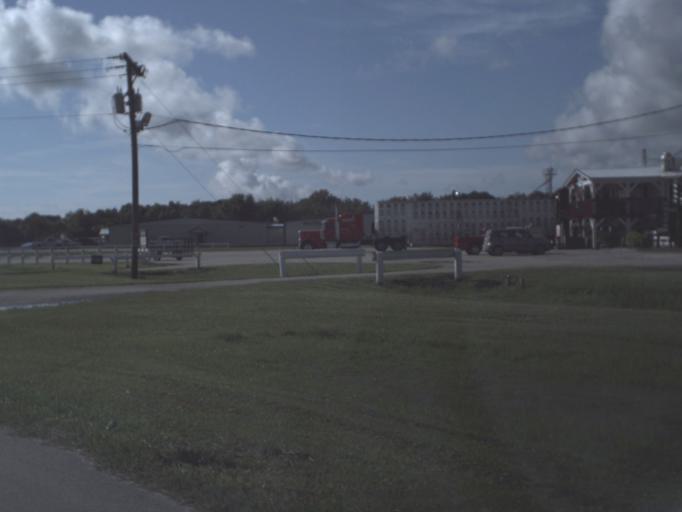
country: US
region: Florida
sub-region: Okeechobee County
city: Okeechobee
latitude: 27.2529
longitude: -80.8535
